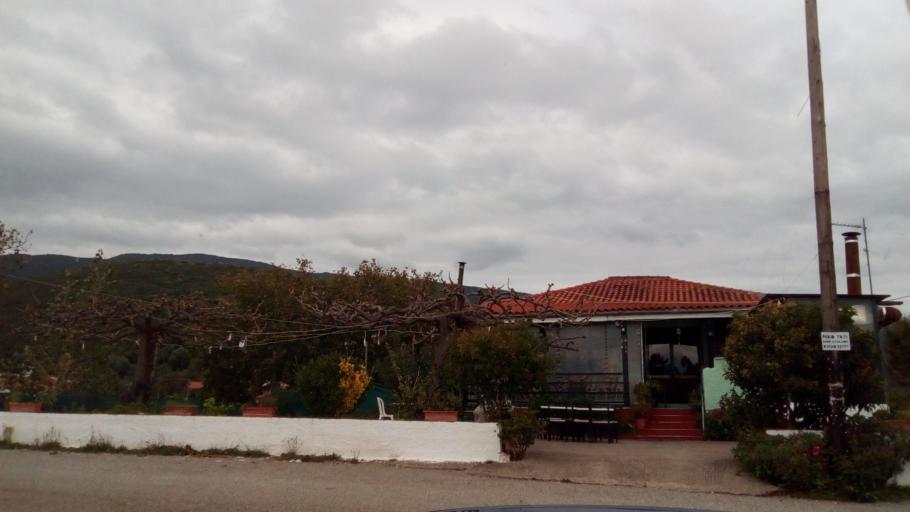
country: GR
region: West Greece
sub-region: Nomos Achaias
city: Kamarai
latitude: 38.4218
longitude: 21.9598
